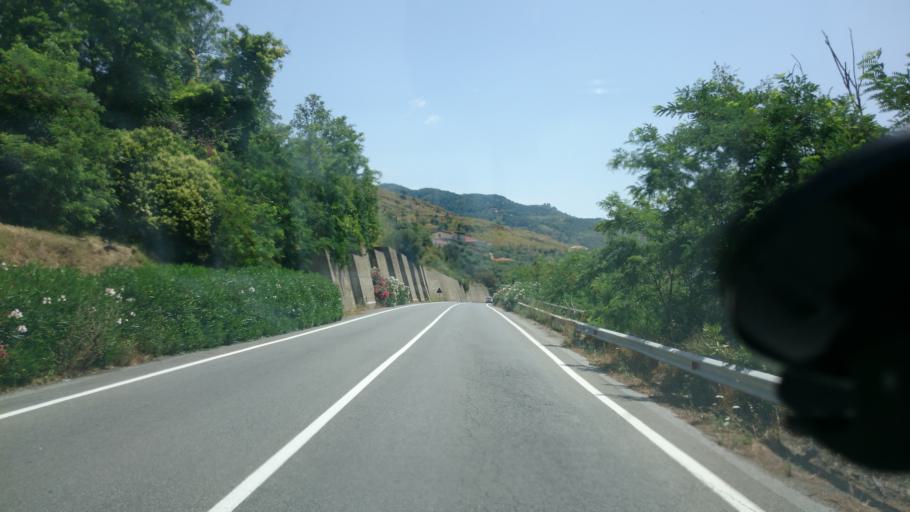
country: IT
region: Calabria
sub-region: Provincia di Cosenza
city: Cittadella del Capo
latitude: 39.5388
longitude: 15.9013
